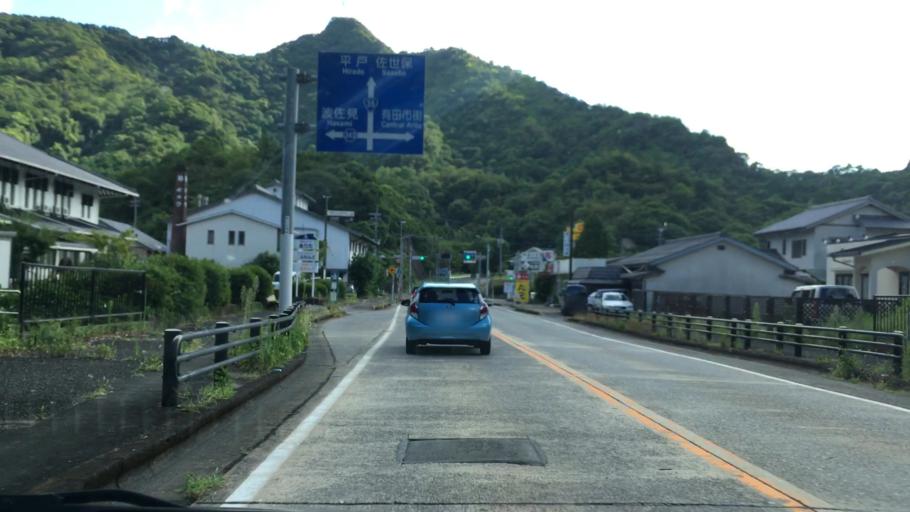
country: JP
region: Saga Prefecture
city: Imaricho-ko
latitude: 33.1902
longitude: 129.9071
